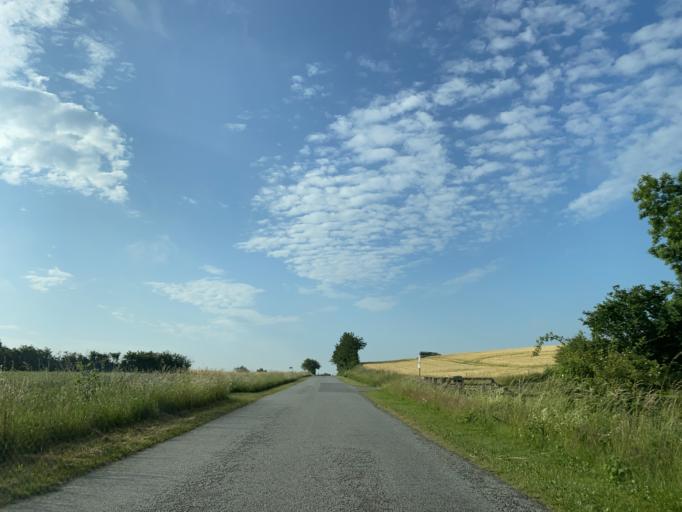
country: DK
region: South Denmark
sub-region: Haderslev Kommune
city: Haderslev
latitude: 55.1830
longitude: 9.4797
